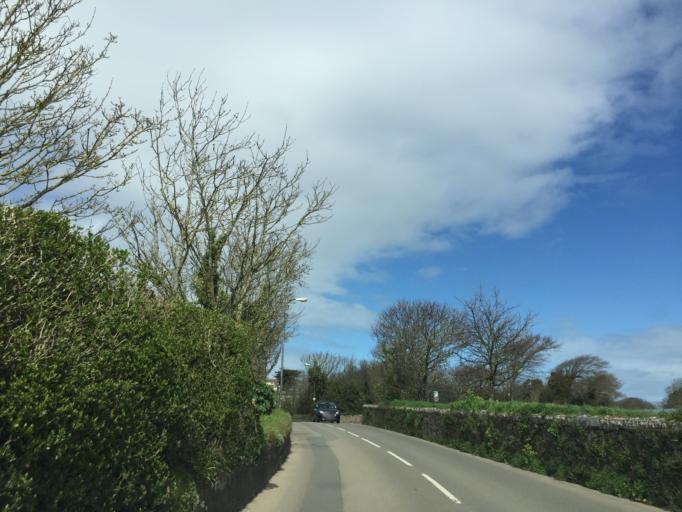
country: JE
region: St Helier
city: Saint Helier
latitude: 49.1775
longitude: -2.1732
